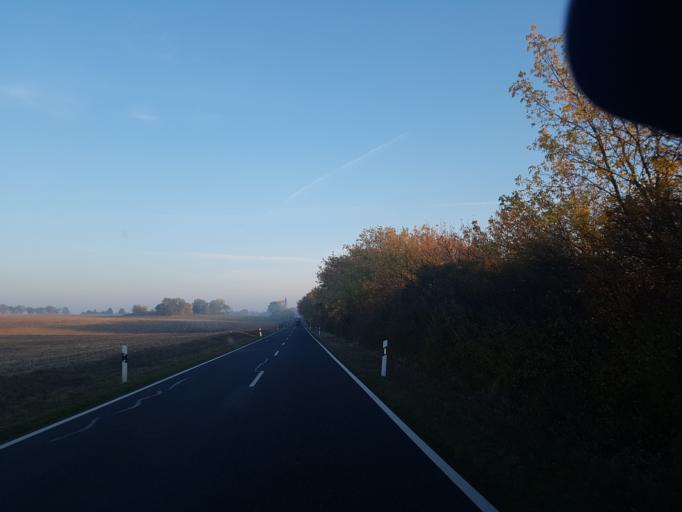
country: DE
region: Brandenburg
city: Juterbog
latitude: 51.9391
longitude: 13.0870
